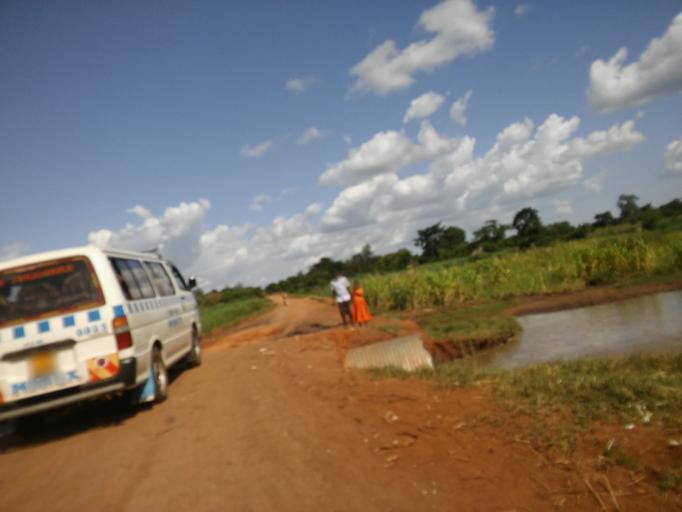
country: UG
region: Eastern Region
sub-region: Pallisa District
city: Pallisa
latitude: 1.1333
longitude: 33.7295
